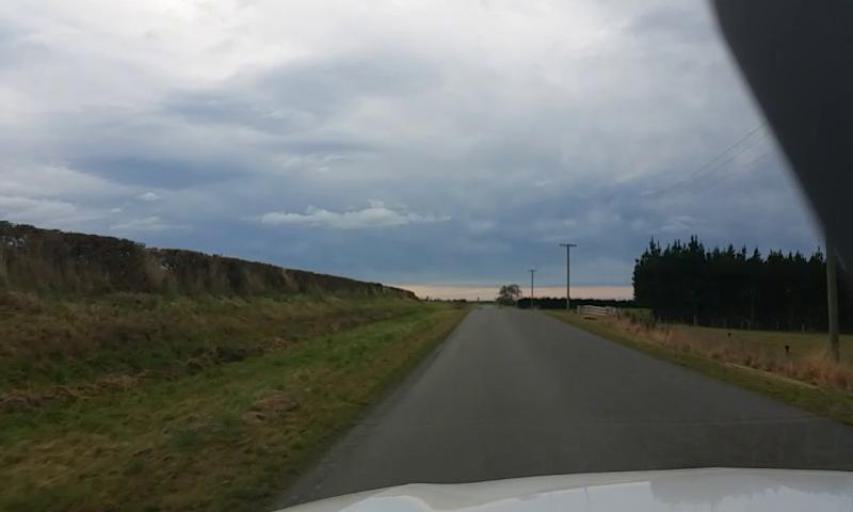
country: NZ
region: Canterbury
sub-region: Waimakariri District
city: Kaiapoi
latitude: -43.2910
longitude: 172.4642
